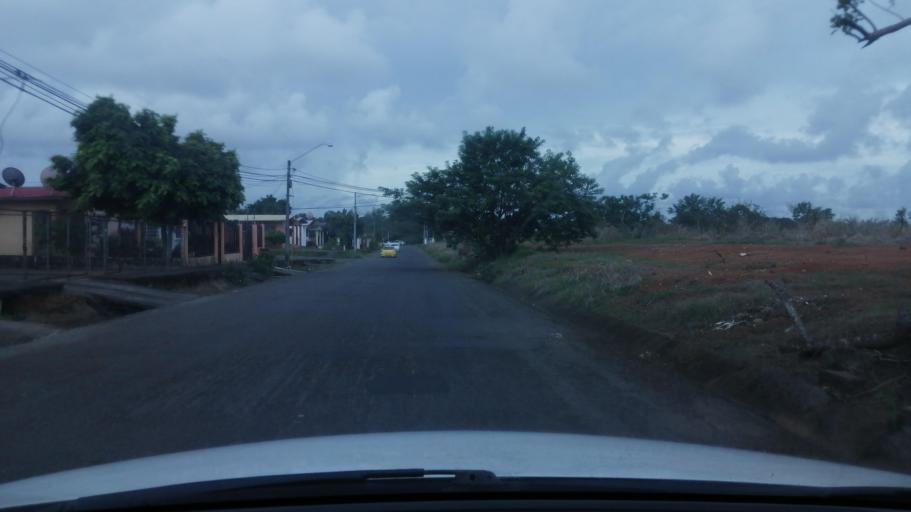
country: PA
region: Chiriqui
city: David
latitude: 8.4037
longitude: -82.4491
